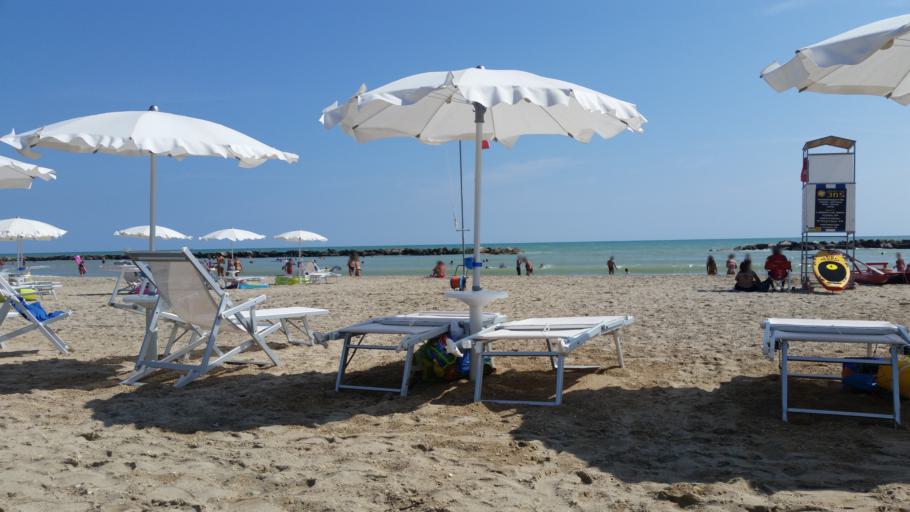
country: IT
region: The Marches
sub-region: Provincia di Ascoli Piceno
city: San Benedetto del Tronto
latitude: 42.9120
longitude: 13.9074
